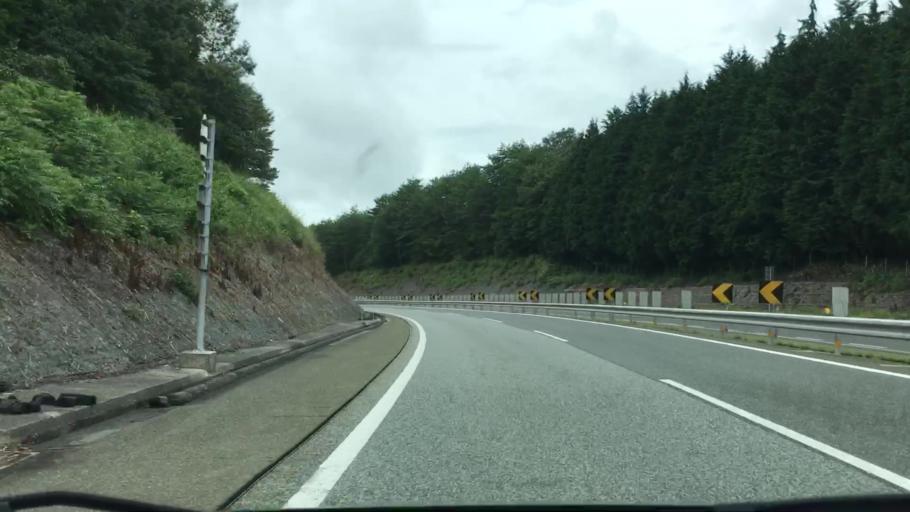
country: JP
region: Hiroshima
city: Shobara
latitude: 34.8730
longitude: 133.1437
